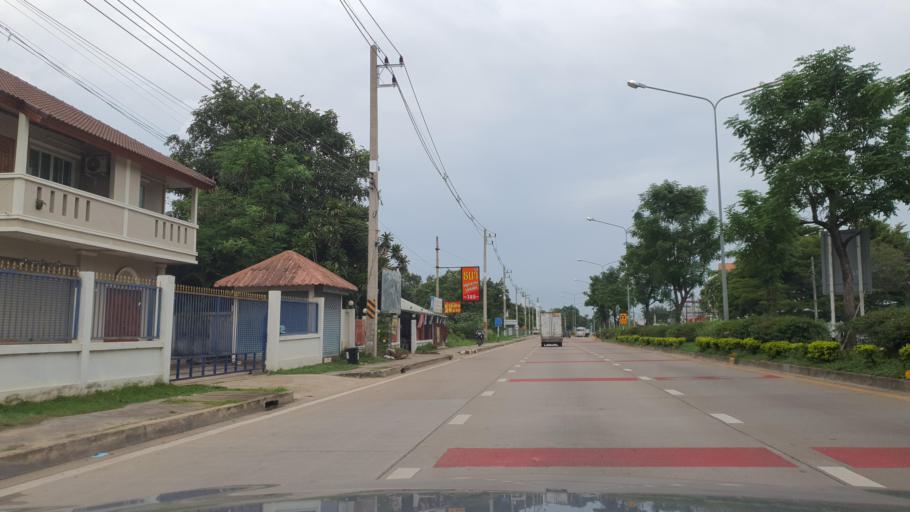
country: TH
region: Chiang Mai
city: Chiang Mai
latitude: 18.7488
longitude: 98.9457
